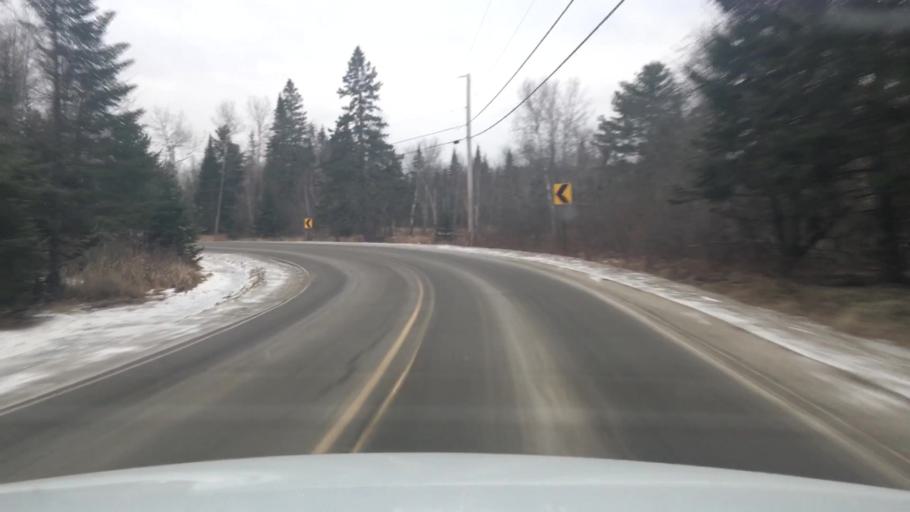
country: US
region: Maine
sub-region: Hancock County
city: Hancock
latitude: 44.5356
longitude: -68.3298
